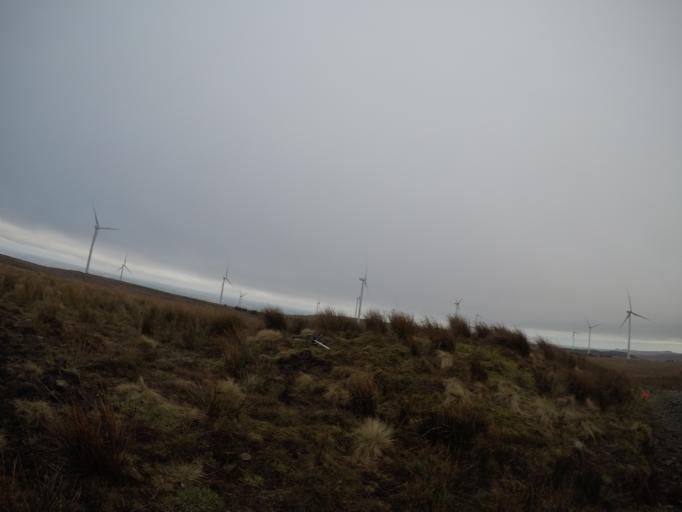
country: GB
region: Scotland
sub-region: North Ayrshire
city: Fairlie
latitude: 55.7418
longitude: -4.7897
